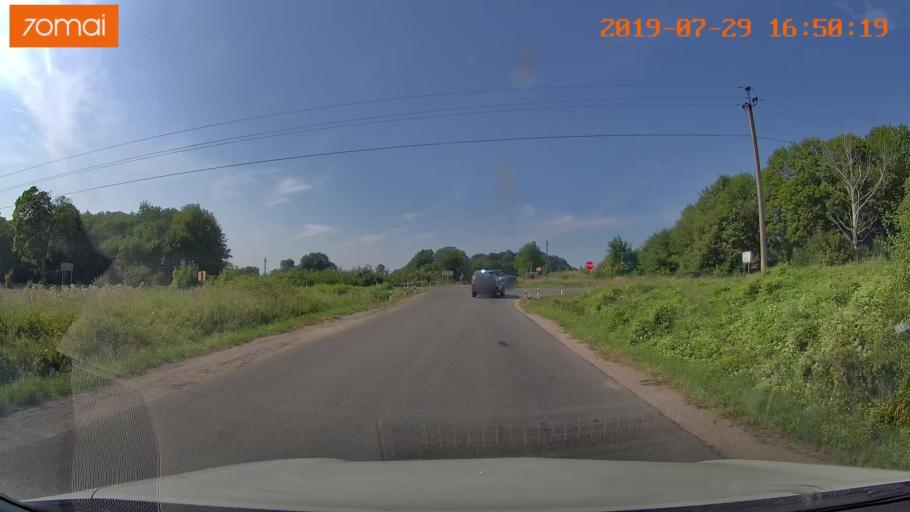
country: RU
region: Kaliningrad
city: Primorsk
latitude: 54.8021
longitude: 20.0565
